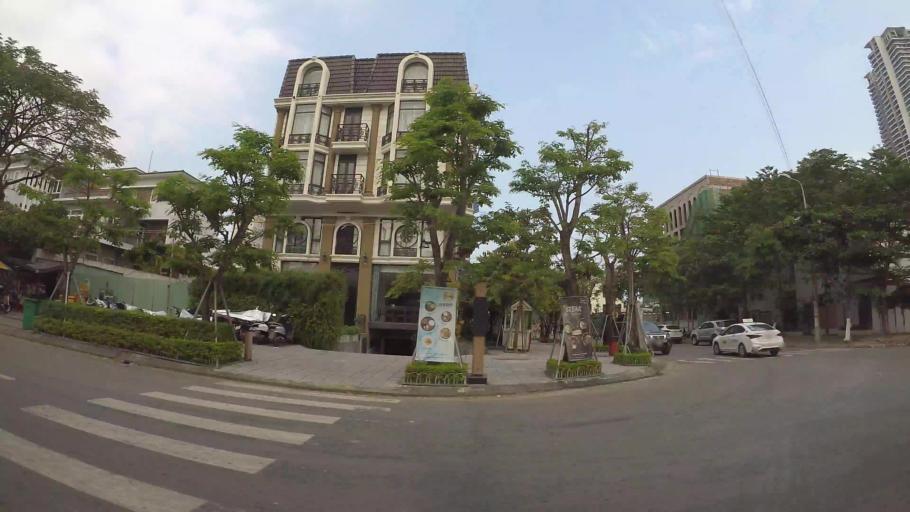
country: VN
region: Da Nang
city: Son Tra
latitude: 16.0737
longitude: 108.2430
